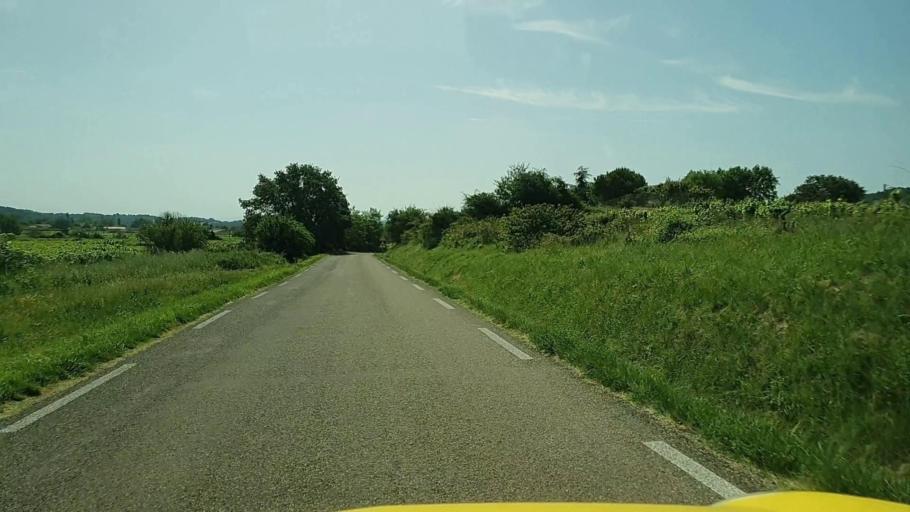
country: FR
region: Languedoc-Roussillon
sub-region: Departement du Gard
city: Sabran
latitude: 44.1189
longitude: 4.5071
